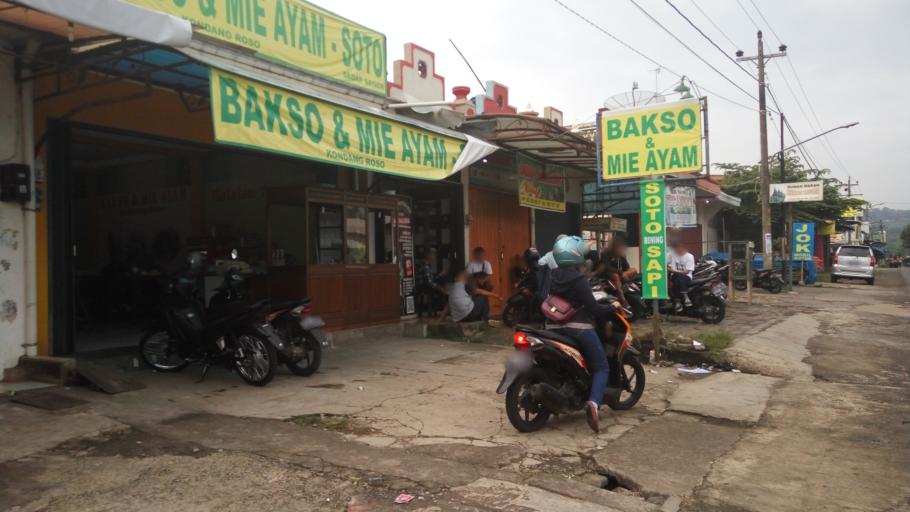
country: ID
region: Central Java
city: Ambarawa
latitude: -7.2472
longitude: 110.4199
